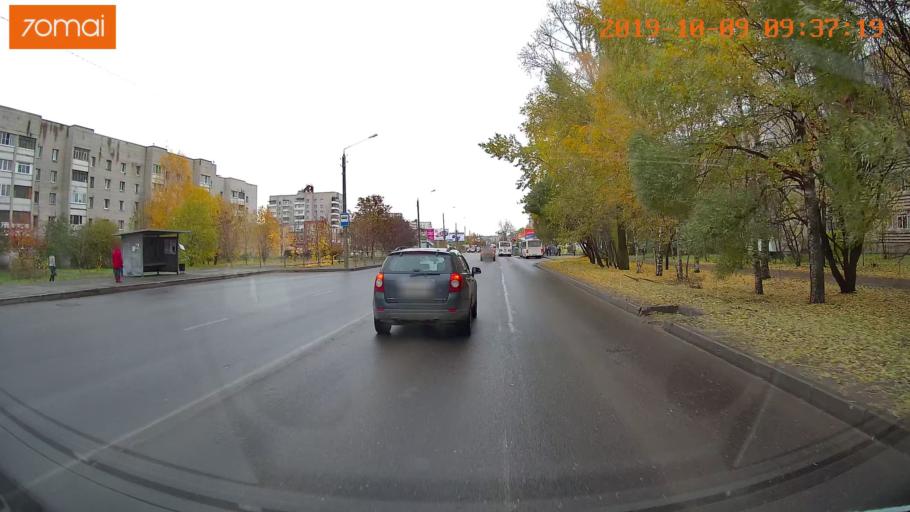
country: RU
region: Vologda
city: Vologda
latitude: 59.1876
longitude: 39.9011
